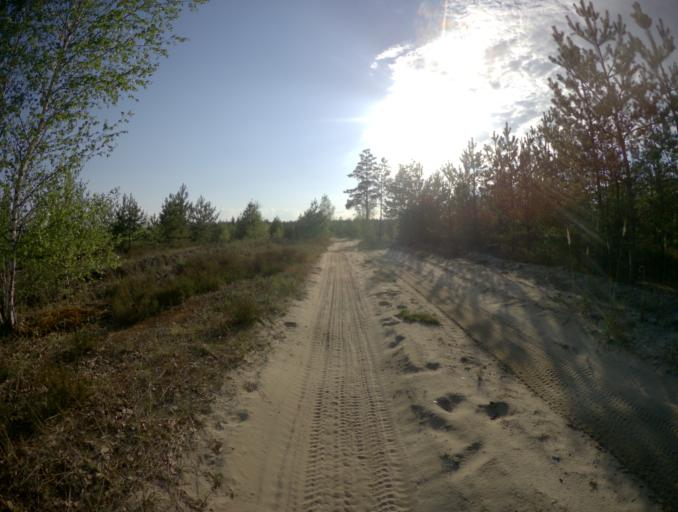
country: RU
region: Vladimir
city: Vyazniki
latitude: 56.4047
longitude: 42.1780
